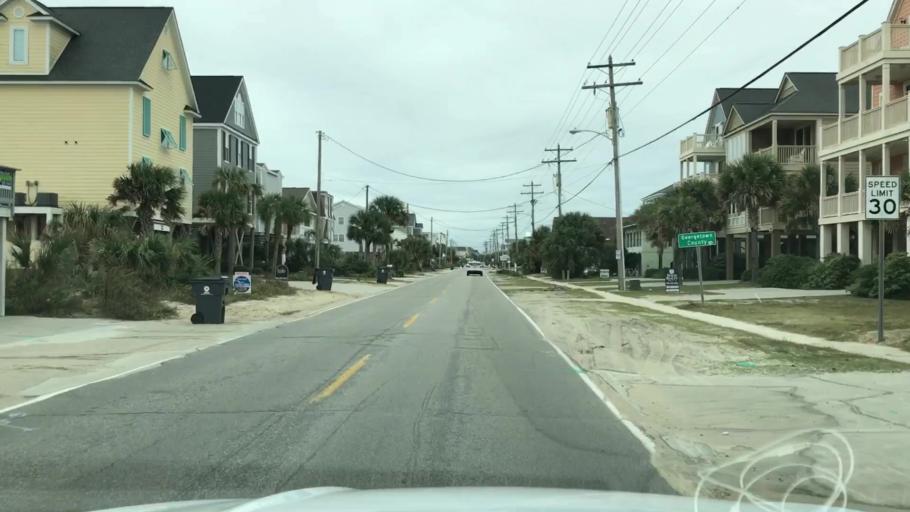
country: US
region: South Carolina
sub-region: Horry County
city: Garden City
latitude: 33.5726
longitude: -79.0023
